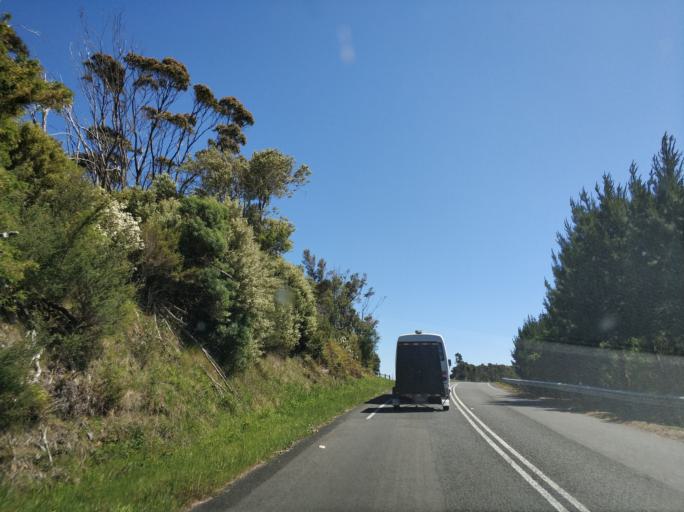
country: AU
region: Victoria
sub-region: Colac-Otway
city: Apollo Bay
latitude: -38.7357
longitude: 143.3040
